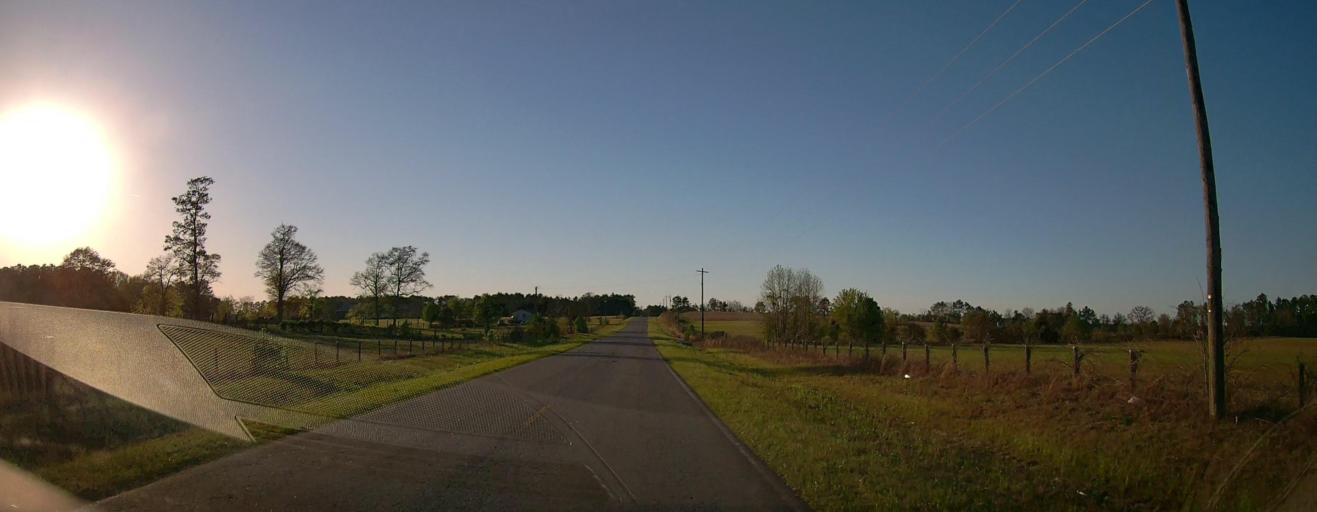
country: US
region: Georgia
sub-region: Wilkinson County
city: Gordon
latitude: 32.8851
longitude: -83.2936
